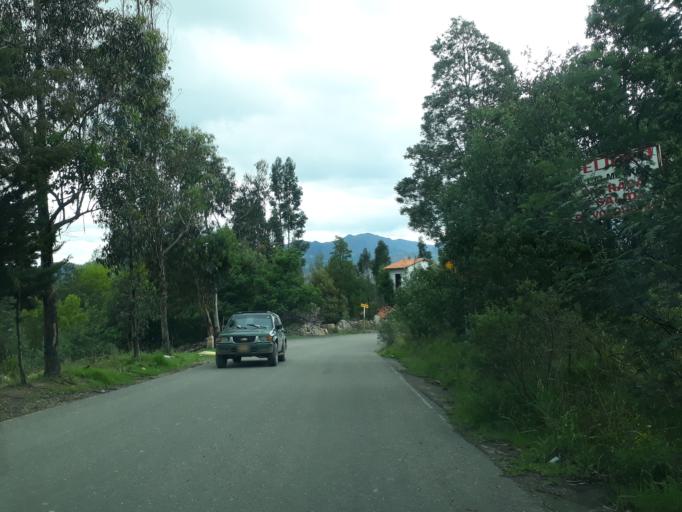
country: CO
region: Cundinamarca
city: Cucunuba
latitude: 5.2365
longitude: -73.7759
